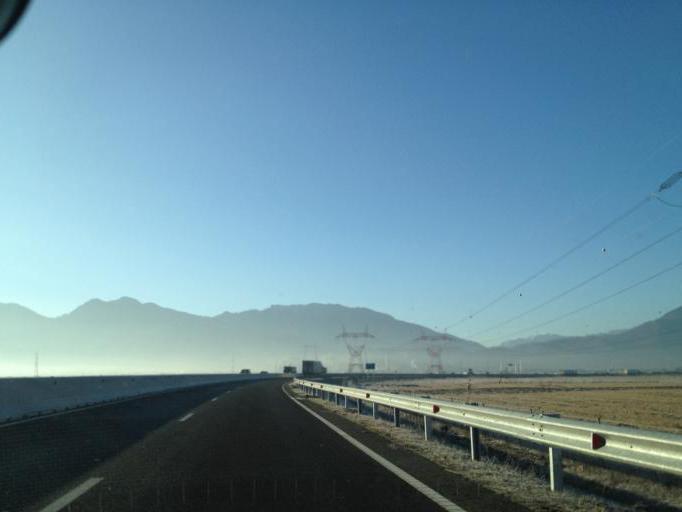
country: RO
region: Brasov
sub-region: Municipiul Sacele
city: Sacele
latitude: 45.6412
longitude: 25.6628
